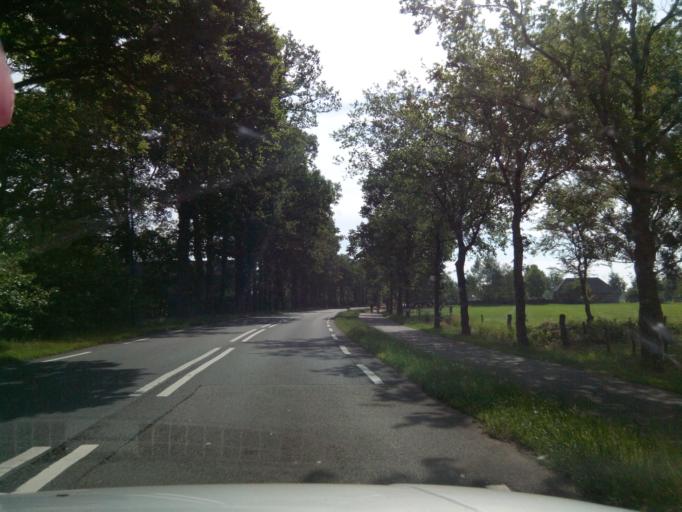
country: NL
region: Utrecht
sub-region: Gemeente Woudenberg
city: Woudenberg
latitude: 52.0837
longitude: 5.3902
